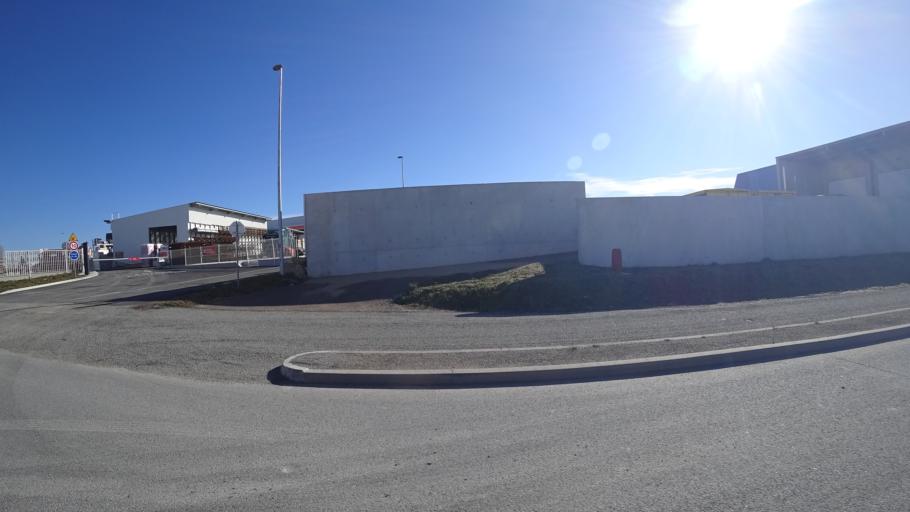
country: FR
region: Midi-Pyrenees
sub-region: Departement de l'Aveyron
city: Sebazac-Concoures
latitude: 44.3895
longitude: 2.5945
